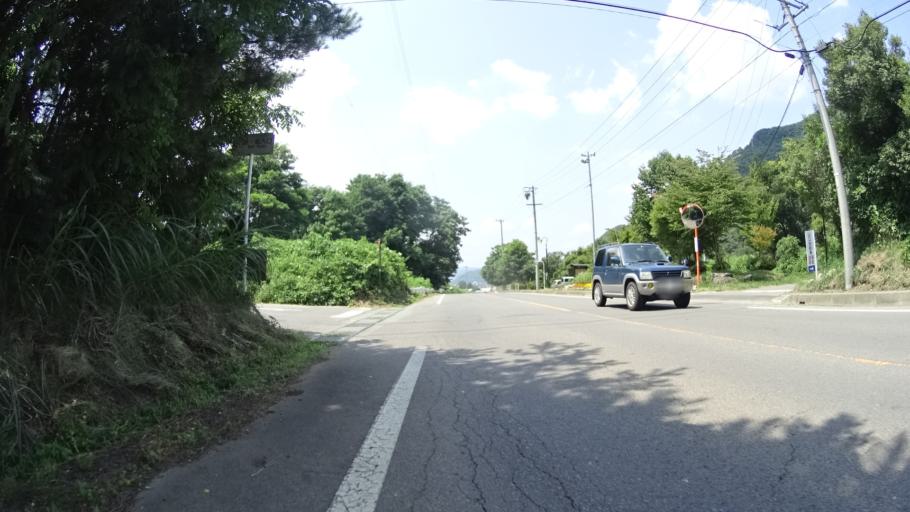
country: JP
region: Nagano
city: Saku
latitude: 36.1427
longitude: 138.5204
